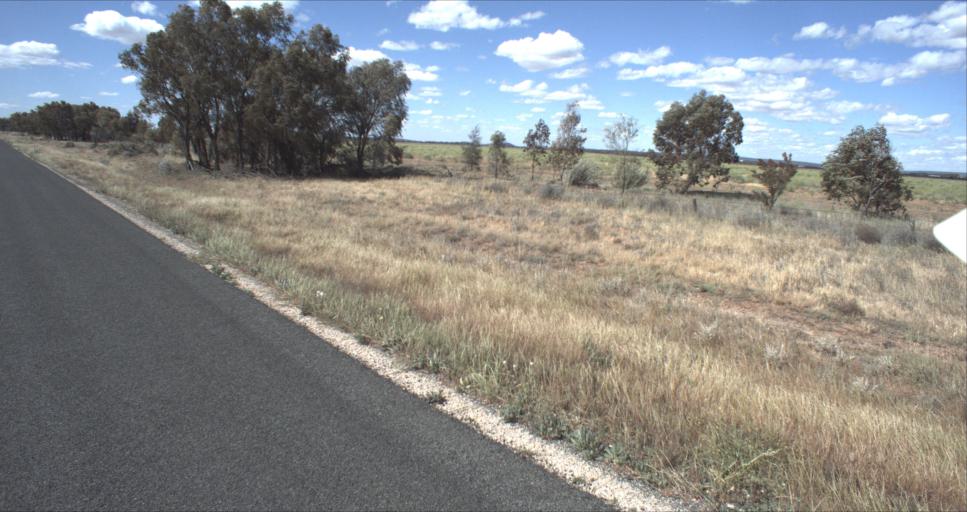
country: AU
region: New South Wales
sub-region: Leeton
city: Leeton
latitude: -34.4376
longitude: 146.2570
